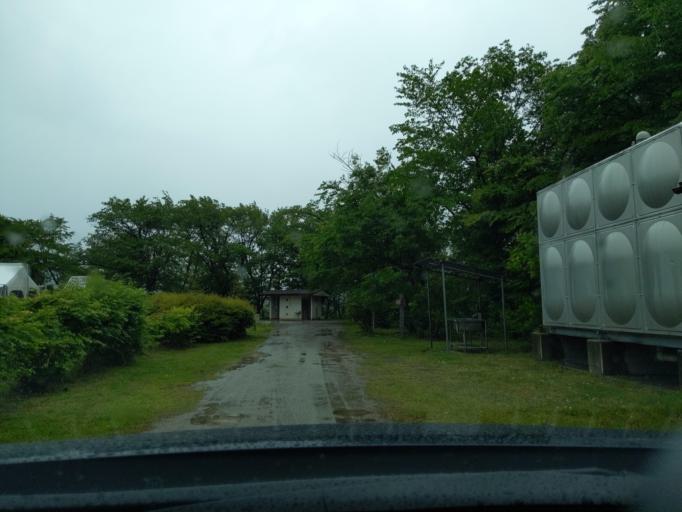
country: JP
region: Fukushima
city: Hobaramachi
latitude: 37.6687
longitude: 140.6498
